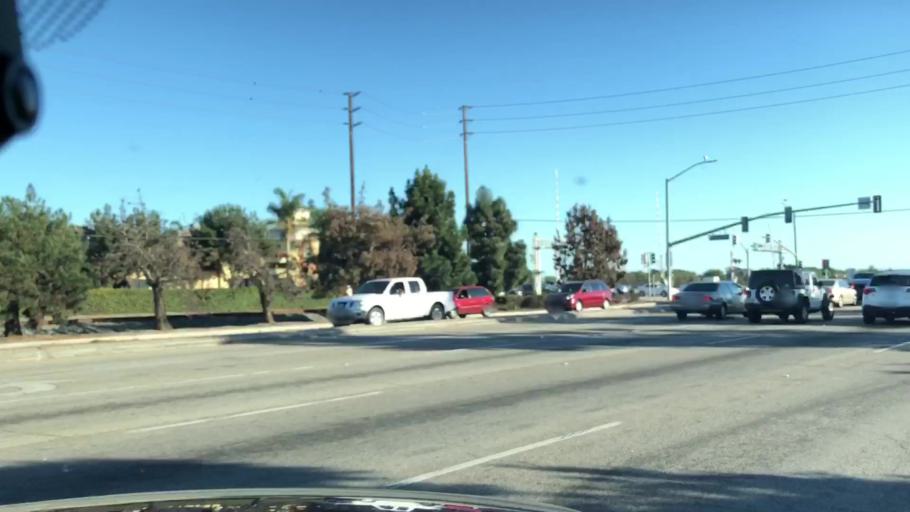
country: US
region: California
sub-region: Ventura County
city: El Rio
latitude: 34.2200
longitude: -119.1773
